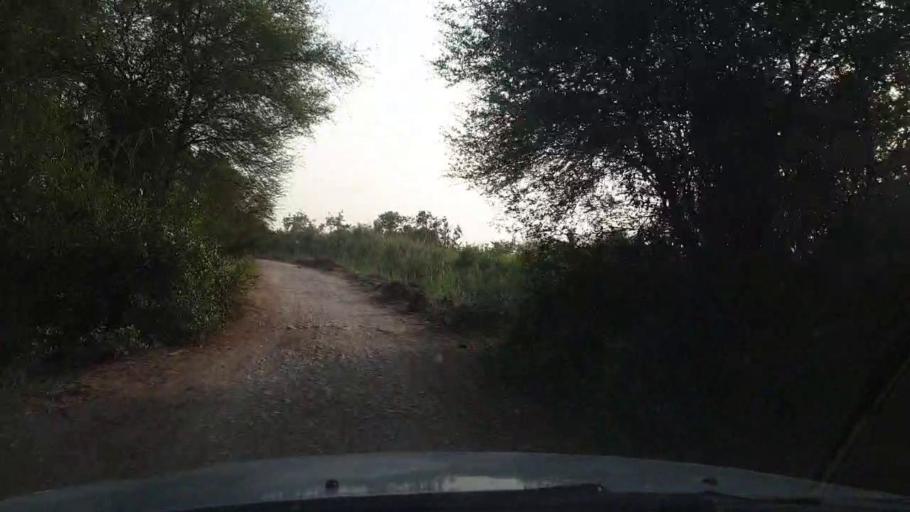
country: PK
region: Sindh
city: Tando Muhammad Khan
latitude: 25.0089
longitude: 68.4361
